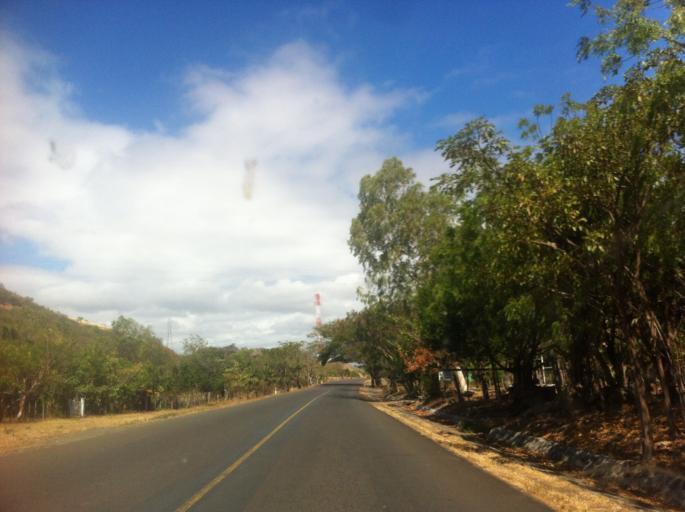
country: NI
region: Chontales
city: Acoyapa
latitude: 12.0176
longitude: -85.2498
